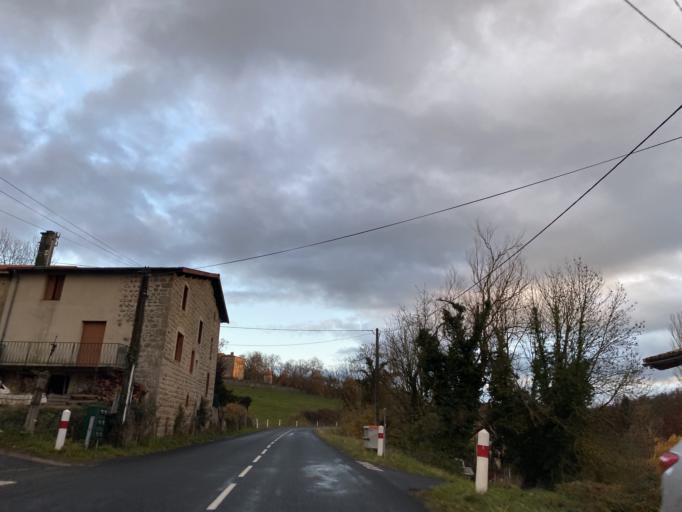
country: FR
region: Auvergne
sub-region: Departement du Puy-de-Dome
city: Cunlhat
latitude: 45.6846
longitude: 3.5766
